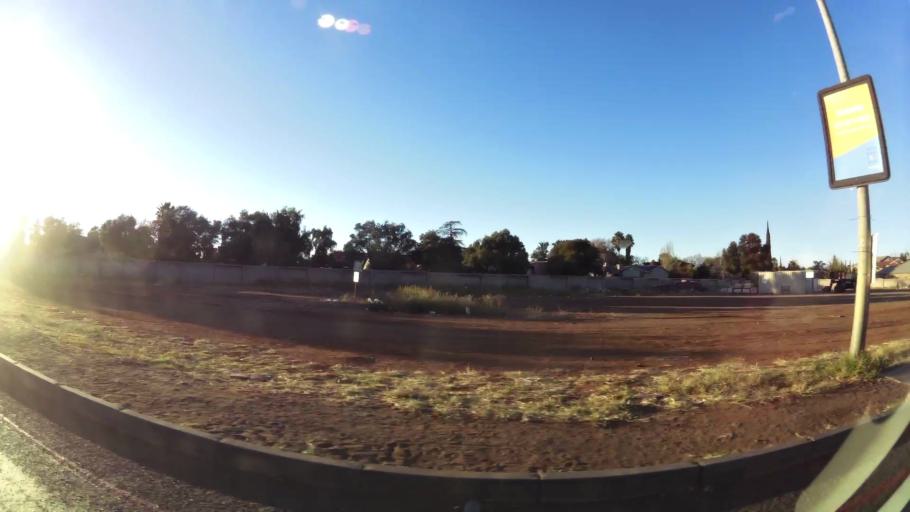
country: ZA
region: Northern Cape
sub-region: Frances Baard District Municipality
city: Kimberley
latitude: -28.7596
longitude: 24.7611
